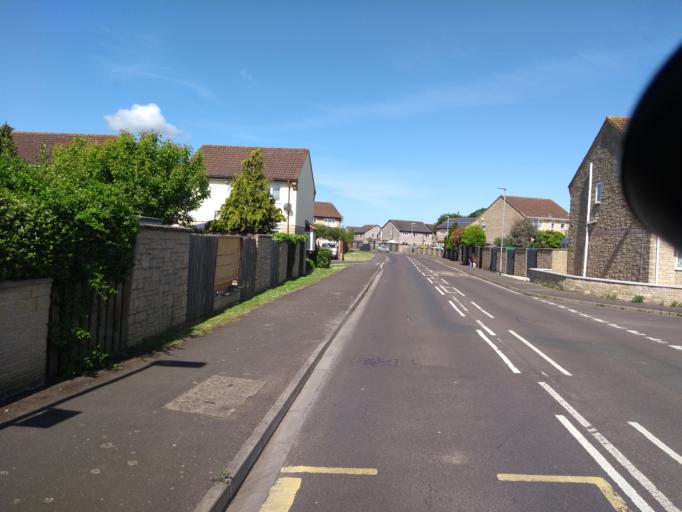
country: GB
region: England
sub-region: Somerset
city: Bridgwater
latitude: 51.1141
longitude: -3.0011
